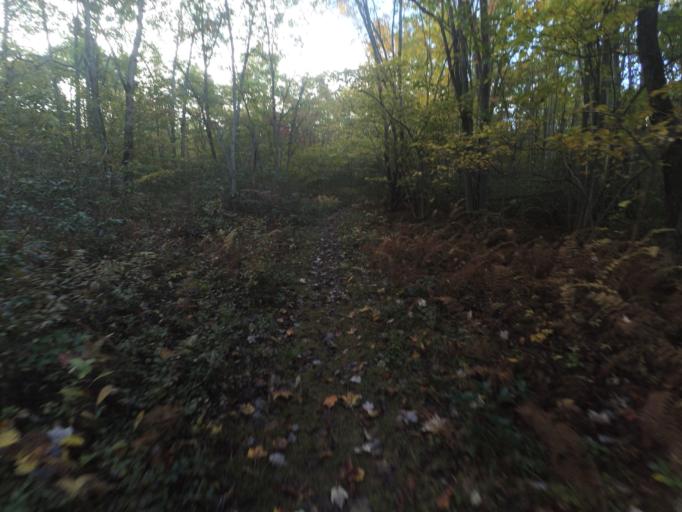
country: US
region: Pennsylvania
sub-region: Centre County
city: Stormstown
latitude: 40.8922
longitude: -78.0011
